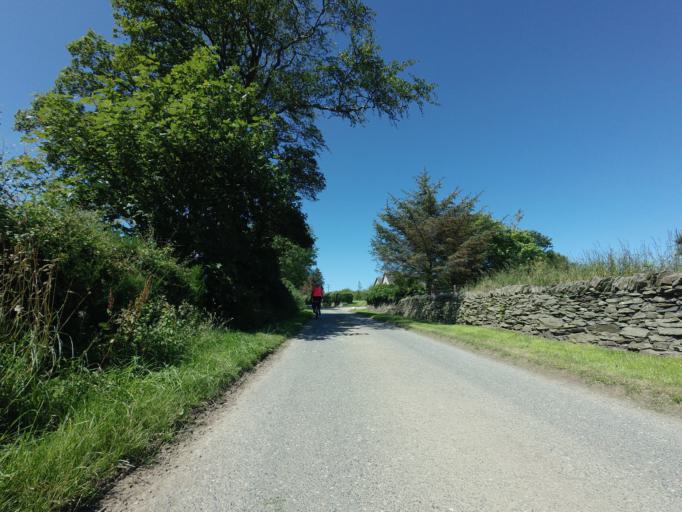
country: GB
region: Scotland
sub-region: Aberdeenshire
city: Macduff
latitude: 57.6375
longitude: -2.4931
